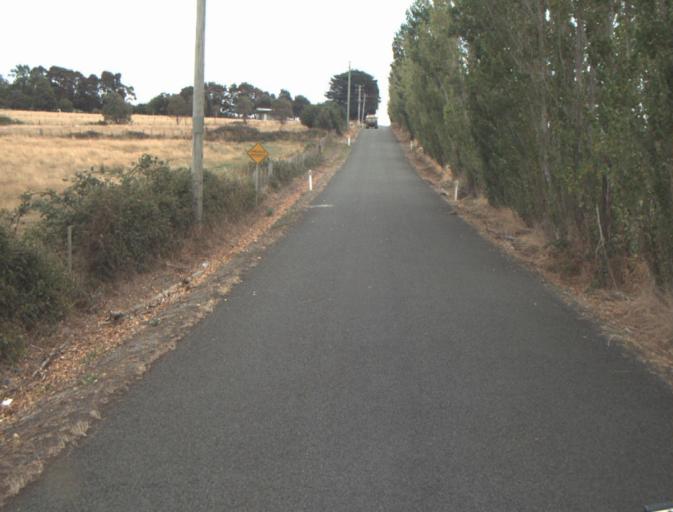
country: AU
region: Tasmania
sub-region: Launceston
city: Mayfield
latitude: -41.2918
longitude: 147.0131
